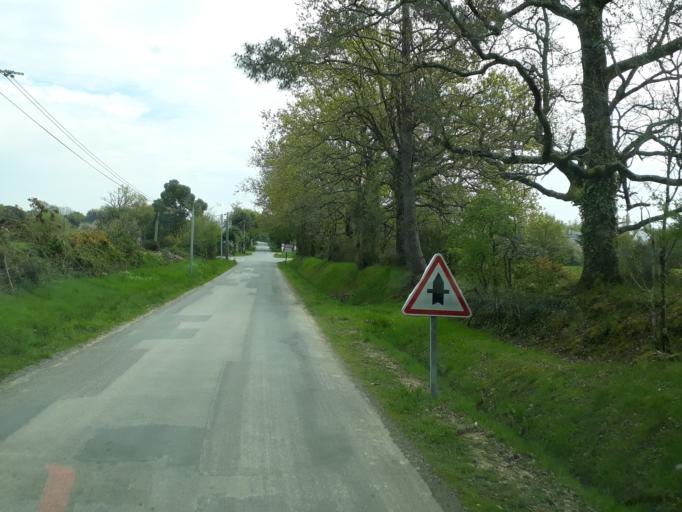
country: FR
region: Brittany
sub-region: Departement du Morbihan
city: Surzur
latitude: 47.5829
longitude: -2.6519
